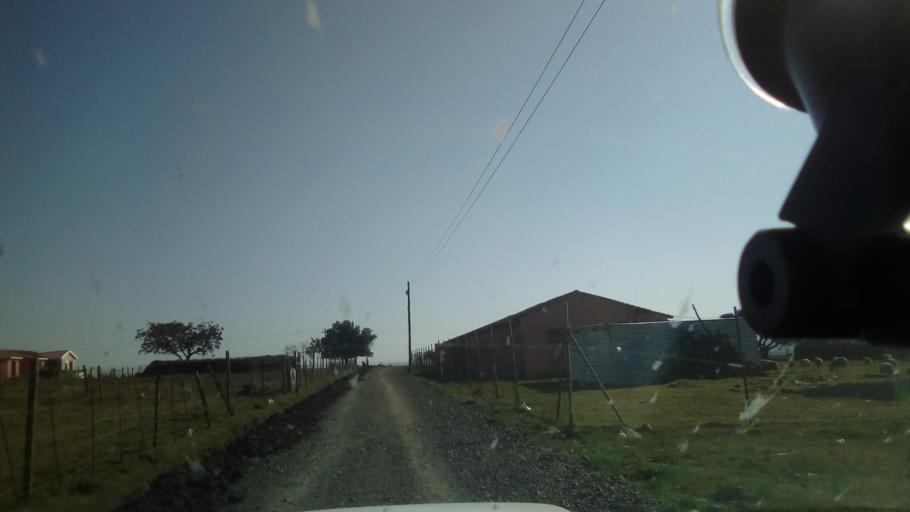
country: ZA
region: Eastern Cape
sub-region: Buffalo City Metropolitan Municipality
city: Bhisho
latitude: -32.9519
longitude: 27.3200
